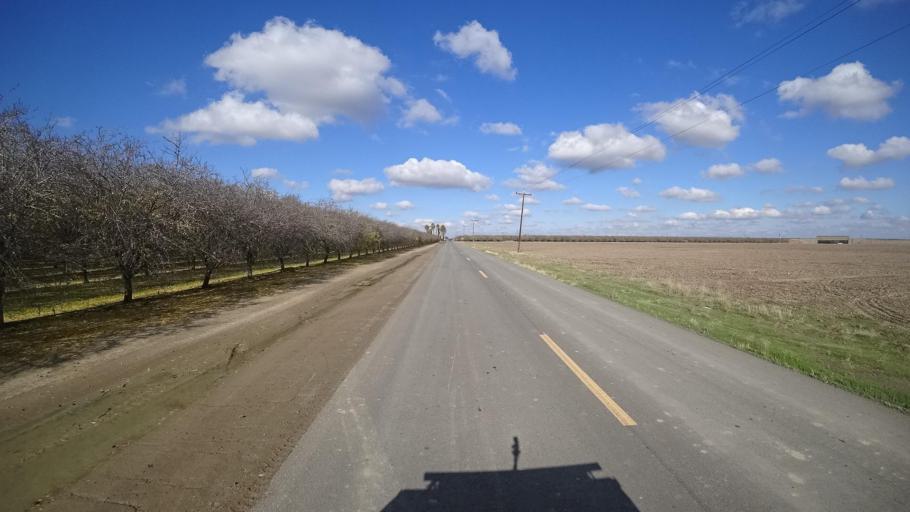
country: US
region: California
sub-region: Kern County
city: Wasco
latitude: 35.7146
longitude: -119.3660
